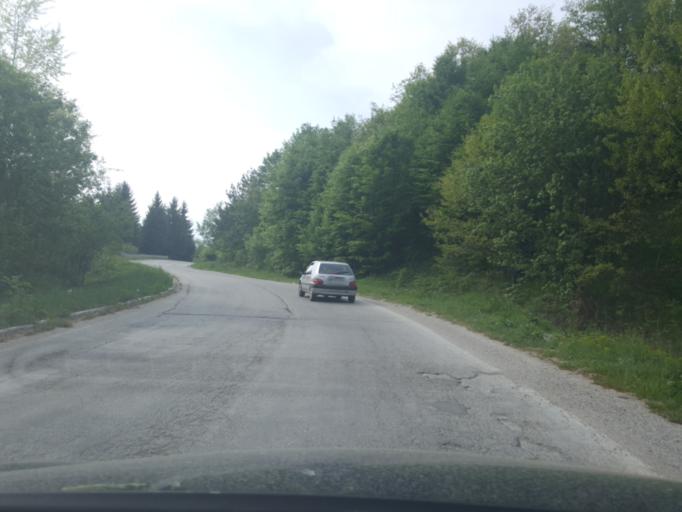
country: RS
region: Central Serbia
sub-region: Zlatiborski Okrug
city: Bajina Basta
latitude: 44.1076
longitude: 19.6649
